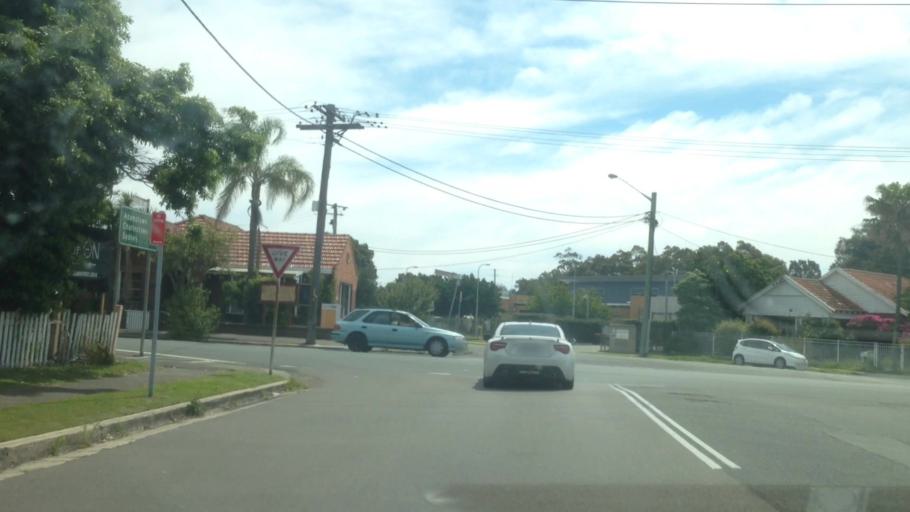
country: AU
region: New South Wales
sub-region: Newcastle
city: Broadmeadow
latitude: -32.9261
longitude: 151.7360
